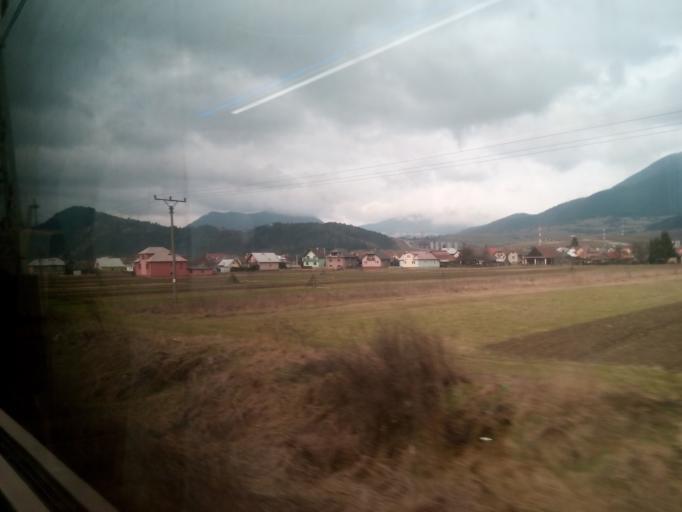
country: SK
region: Zilinsky
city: Ruzomberok
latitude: 49.0898
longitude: 19.3632
